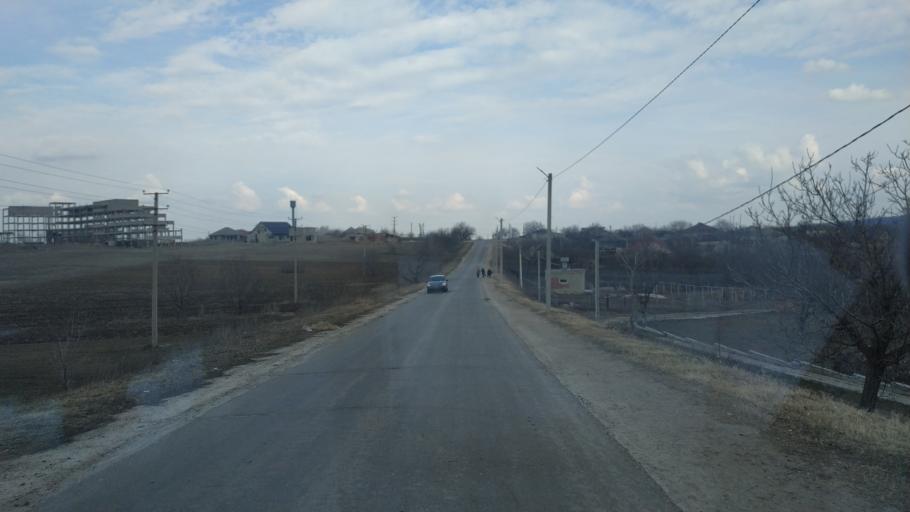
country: MD
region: Anenii Noi
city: Anenii Noi
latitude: 46.9016
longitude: 29.3141
